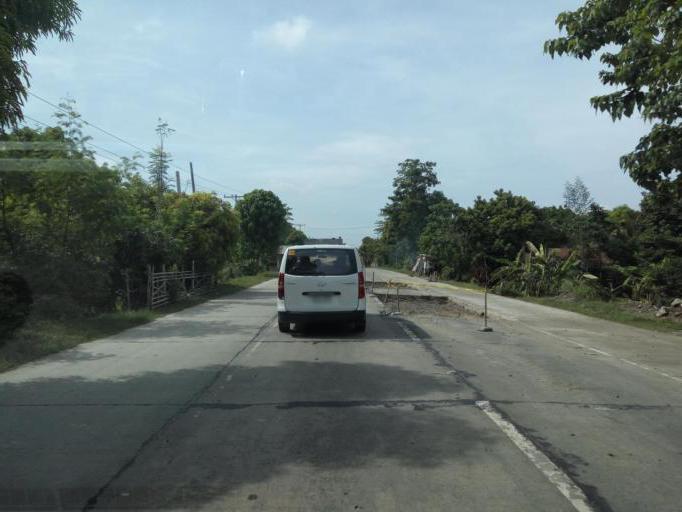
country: PH
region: Cagayan Valley
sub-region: Province of Isabela
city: Gamu
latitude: 17.0513
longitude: 121.8579
